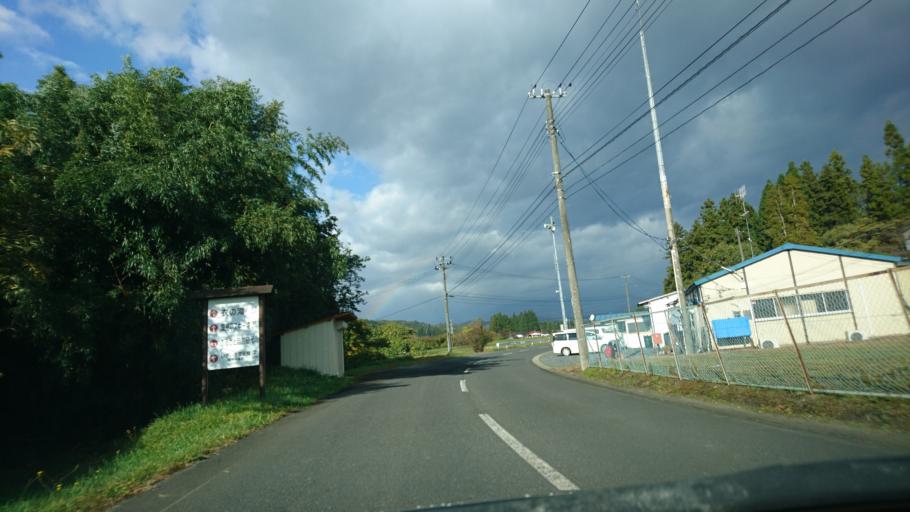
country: JP
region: Iwate
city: Mizusawa
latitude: 39.0736
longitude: 141.0145
